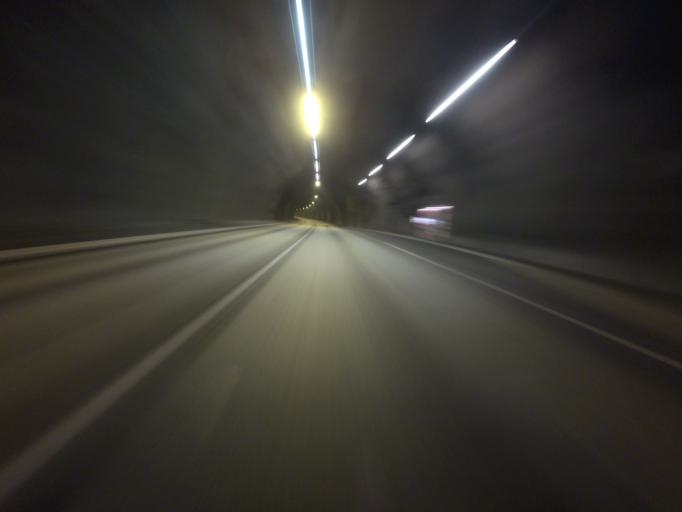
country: FO
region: Eysturoy
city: Eystur
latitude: 62.2045
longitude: -6.6729
